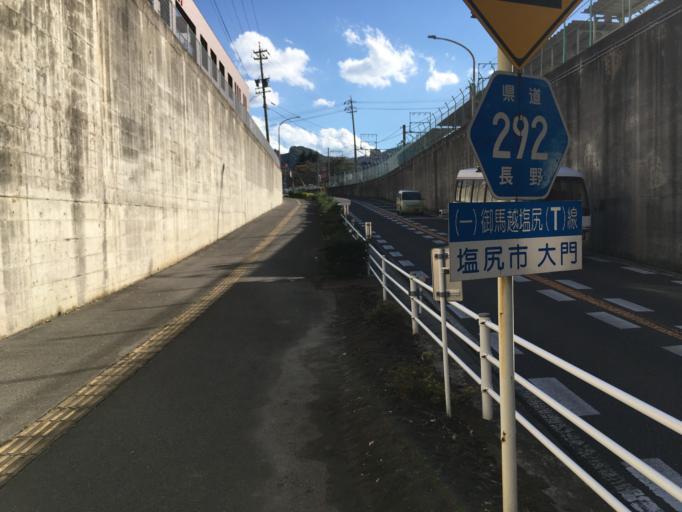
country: JP
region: Nagano
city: Shiojiri
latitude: 36.1135
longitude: 137.9481
